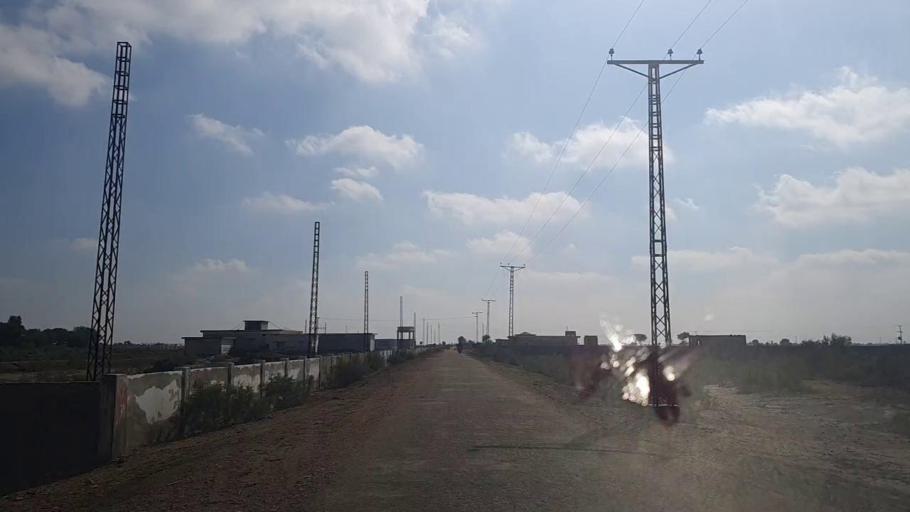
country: PK
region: Sindh
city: Sanghar
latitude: 26.0659
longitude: 69.0042
